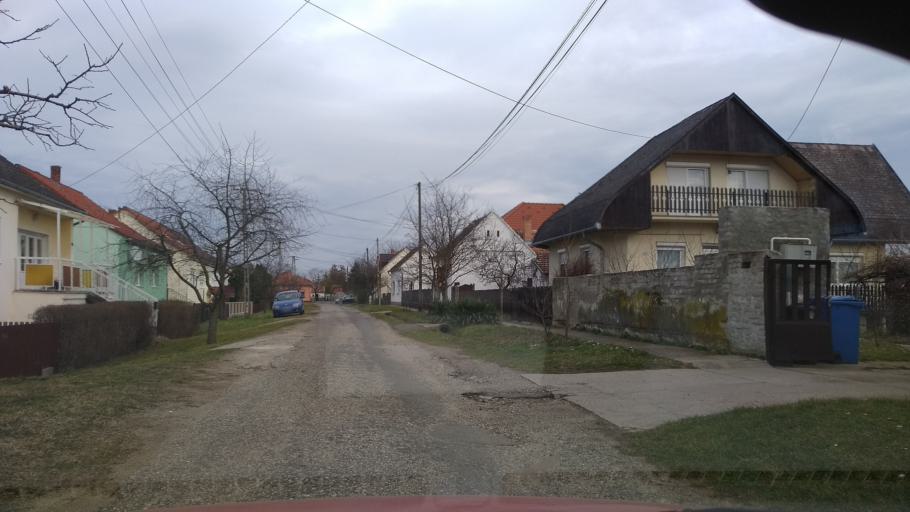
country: HU
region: Somogy
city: Barcs
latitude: 45.9566
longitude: 17.4456
